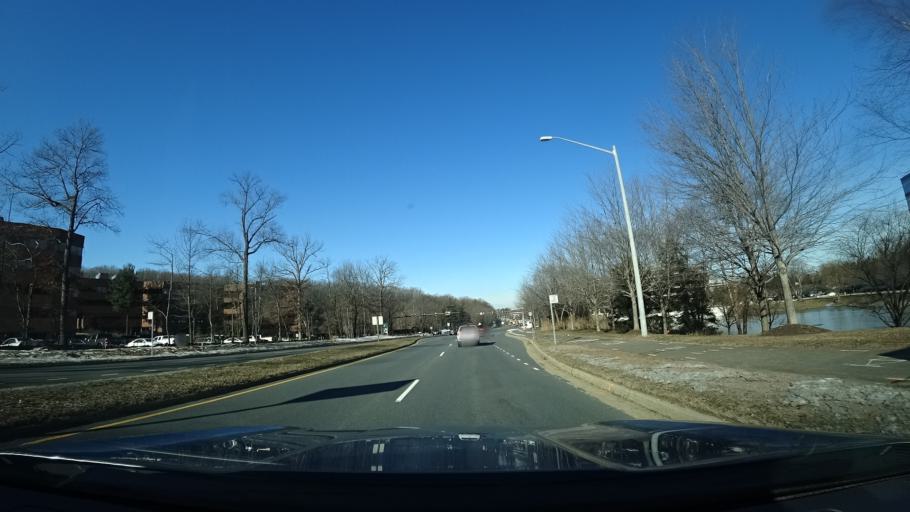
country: US
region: Virginia
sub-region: Fairfax County
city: Reston
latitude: 38.9465
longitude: -77.3599
